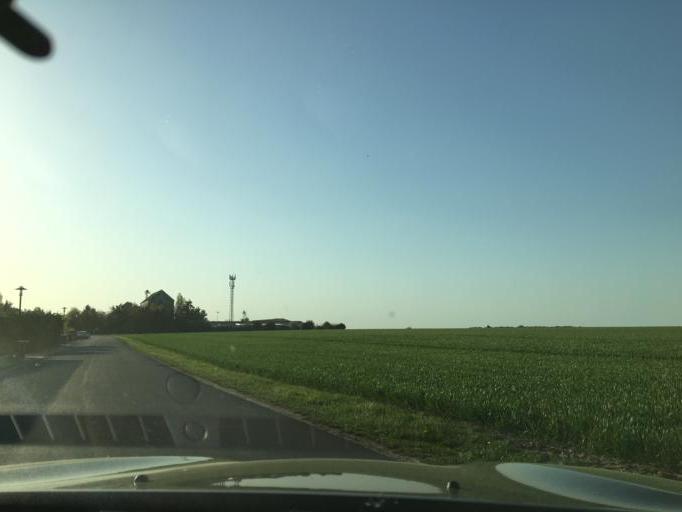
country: FR
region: Centre
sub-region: Departement du Loir-et-Cher
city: Ouzouer-le-Marche
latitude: 47.9134
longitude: 1.5317
